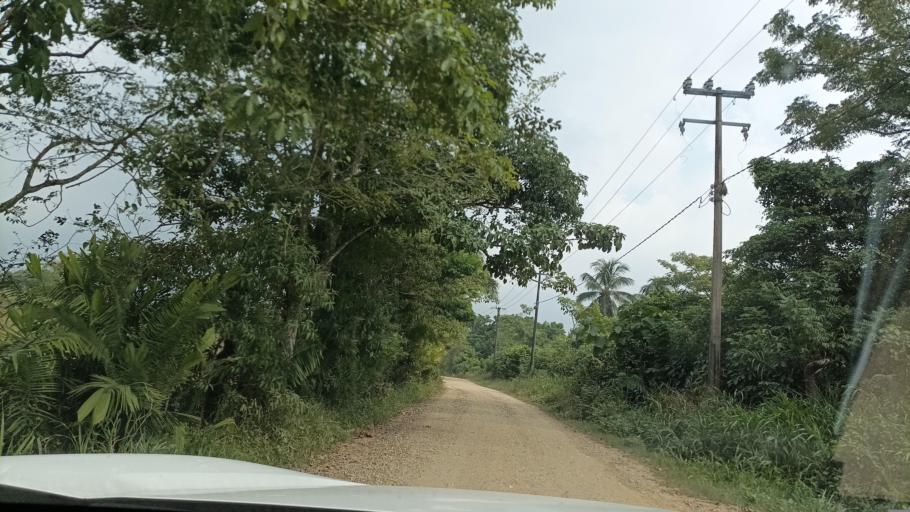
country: MX
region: Veracruz
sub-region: Moloacan
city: Cuichapa
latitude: 17.5874
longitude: -94.2044
